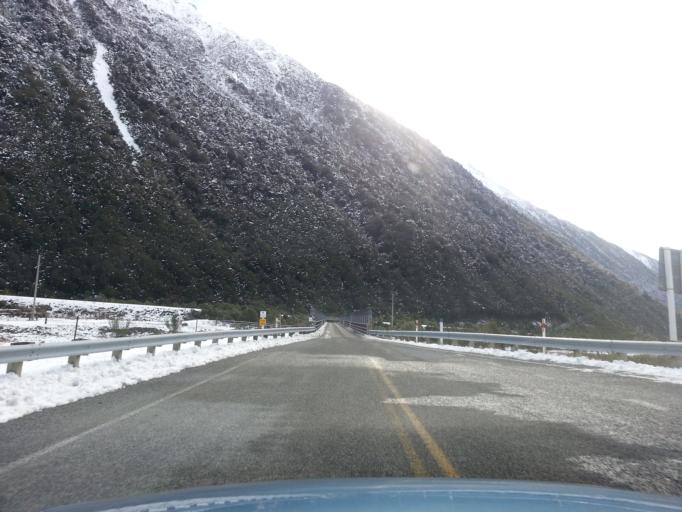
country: NZ
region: West Coast
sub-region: Grey District
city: Greymouth
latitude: -42.8517
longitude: 171.5606
